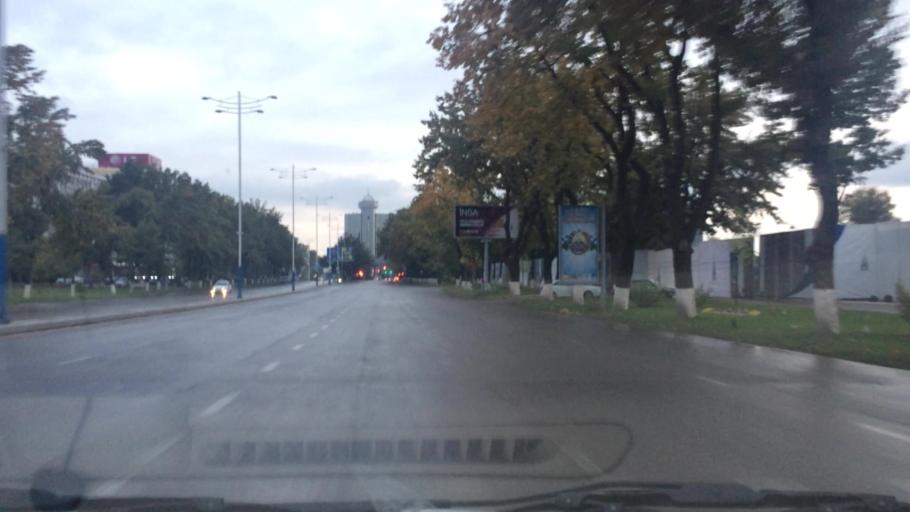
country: UZ
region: Toshkent Shahri
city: Tashkent
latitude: 41.3117
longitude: 69.2477
